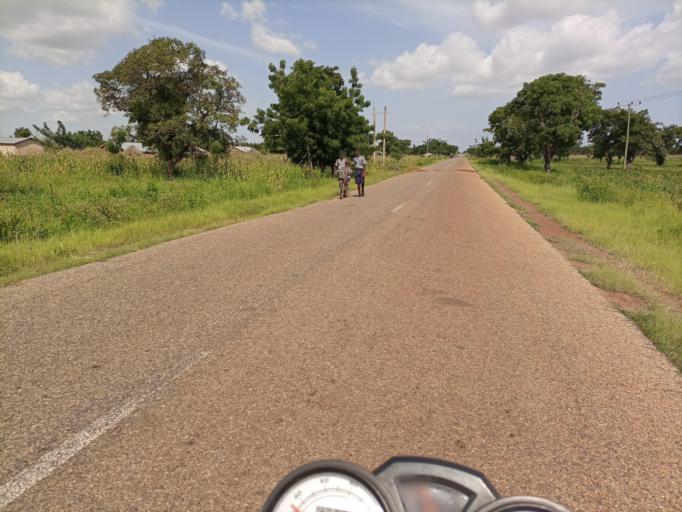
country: GH
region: Northern
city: Savelugu
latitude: 9.5734
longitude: -1.0104
